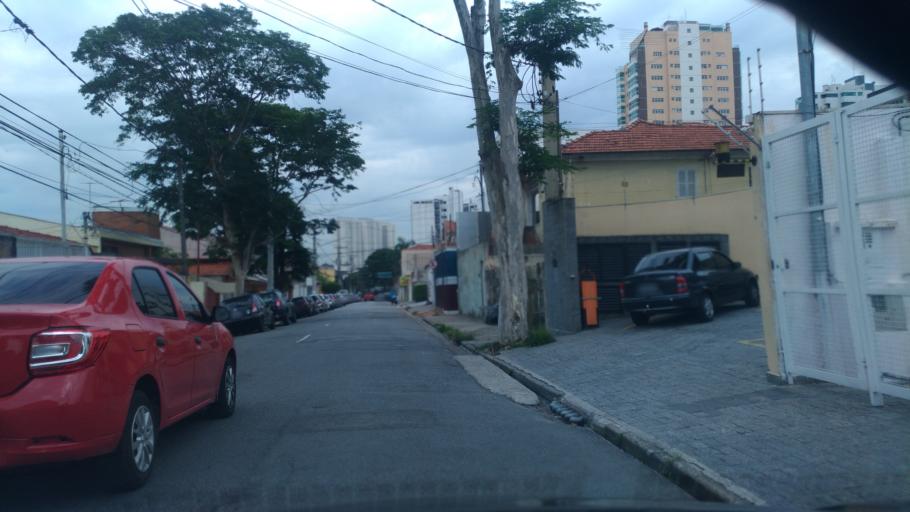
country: BR
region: Sao Paulo
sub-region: Sao Bernardo Do Campo
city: Sao Bernardo do Campo
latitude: -23.7061
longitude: -46.5473
